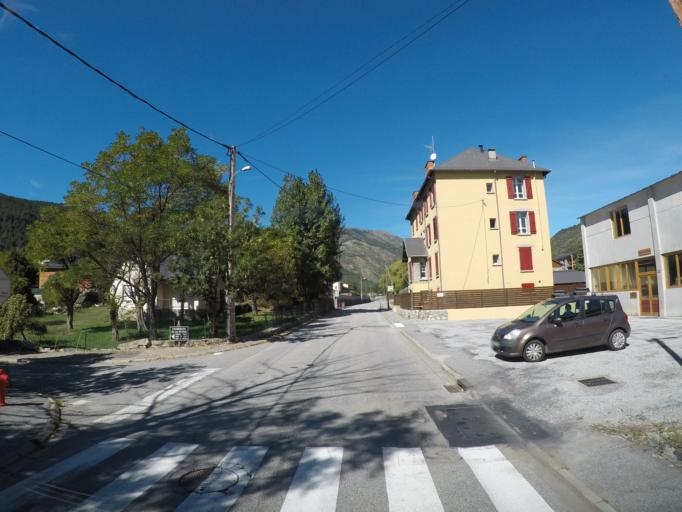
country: ES
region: Catalonia
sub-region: Provincia de Girona
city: Guils de Cerdanya
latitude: 42.4662
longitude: 1.8872
